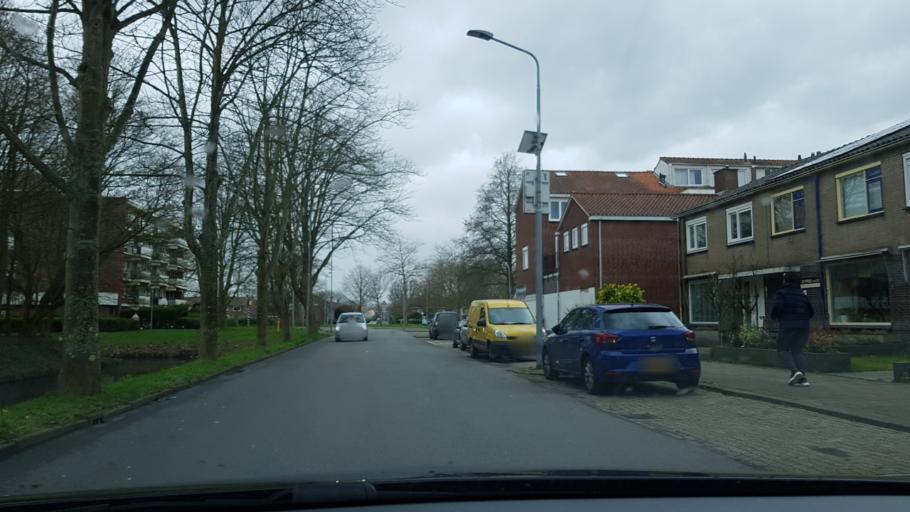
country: NL
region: North Holland
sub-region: Gemeente Haarlemmermeer
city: Hoofddorp
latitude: 52.3122
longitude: 4.6885
